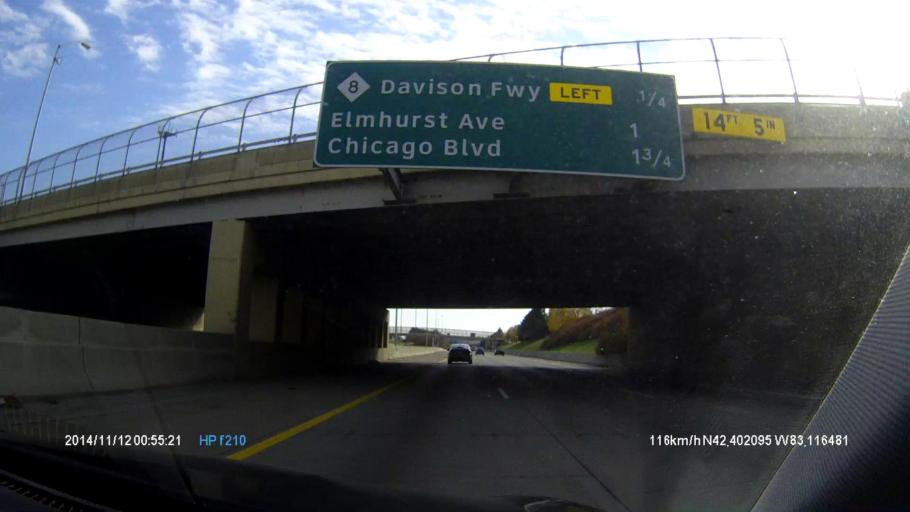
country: US
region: Michigan
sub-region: Wayne County
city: Highland Park
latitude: 42.4021
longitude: -83.1164
